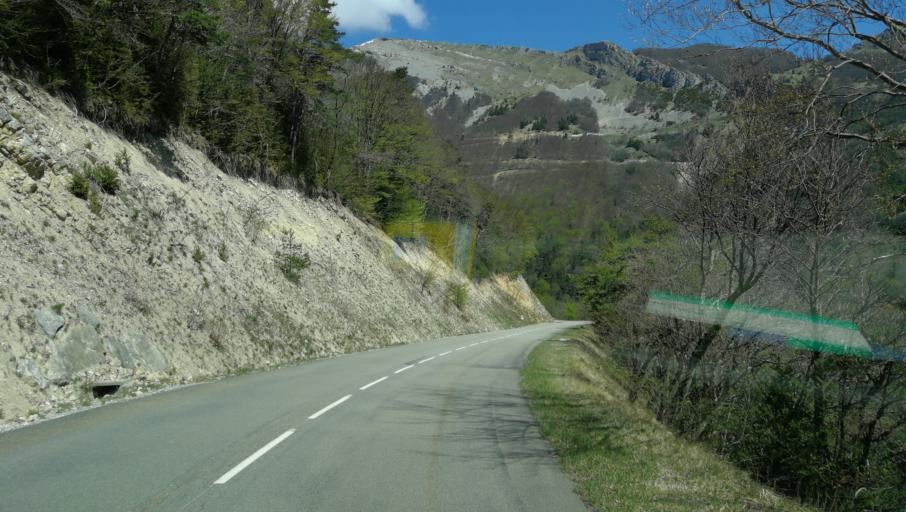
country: FR
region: Rhone-Alpes
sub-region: Departement de la Drome
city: Die
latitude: 44.8287
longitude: 5.3916
